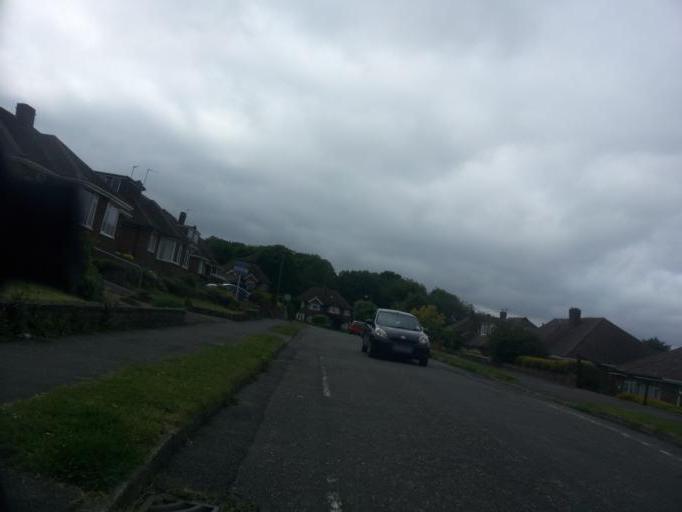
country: GB
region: England
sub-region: Kent
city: Maidstone
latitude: 51.2781
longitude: 0.4975
